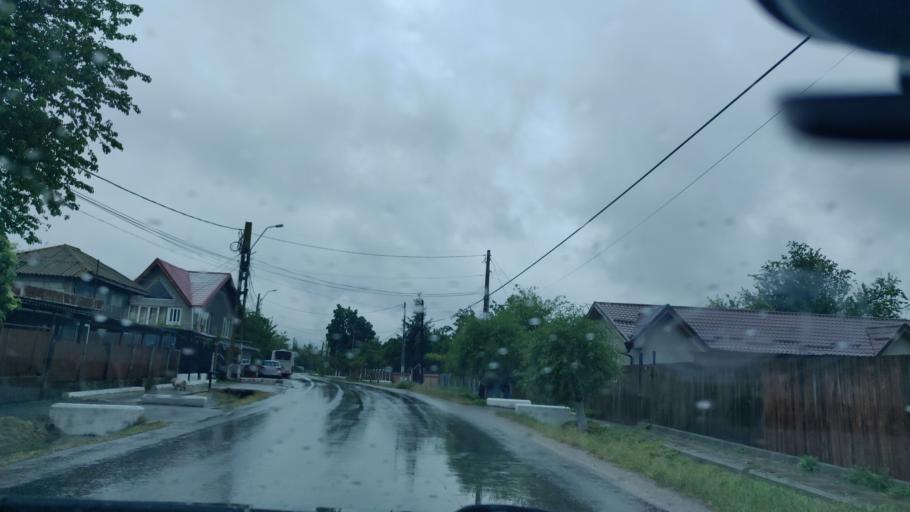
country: RO
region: Giurgiu
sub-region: Comuna Bulbucata
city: Bulbucata
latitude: 44.2796
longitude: 25.8195
